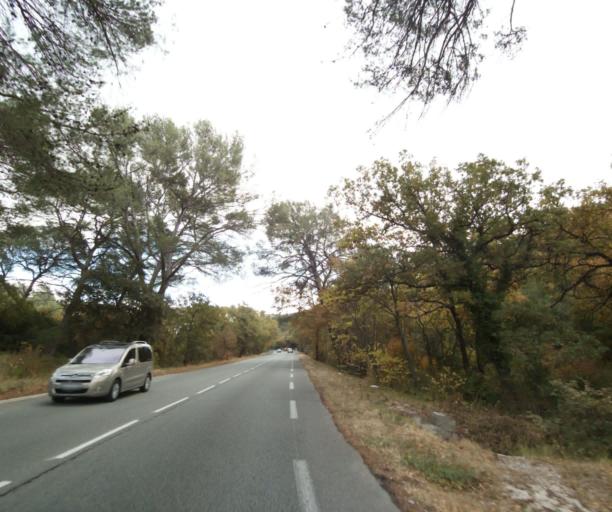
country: FR
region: Provence-Alpes-Cote d'Azur
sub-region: Departement des Bouches-du-Rhone
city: Cuges-les-Pins
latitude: 43.2655
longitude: 5.6636
